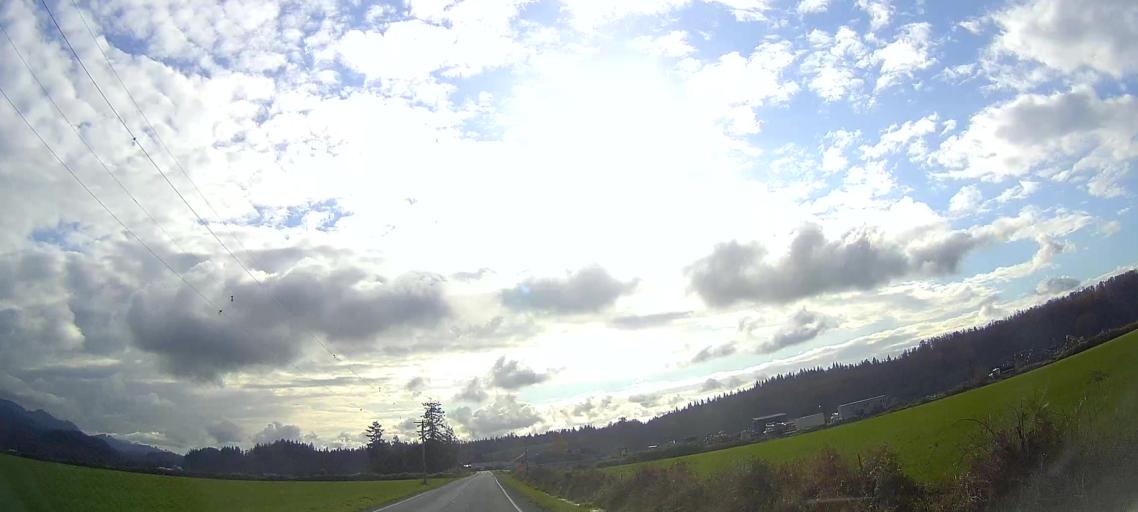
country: US
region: Washington
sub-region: Skagit County
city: Clear Lake
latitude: 48.4370
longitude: -122.2209
